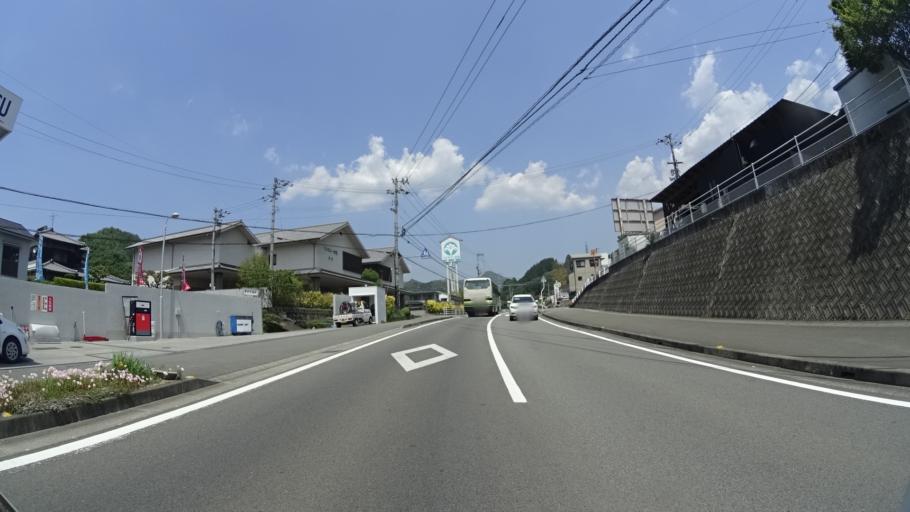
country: JP
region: Ehime
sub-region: Shikoku-chuo Shi
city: Matsuyama
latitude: 33.8558
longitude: 132.8105
